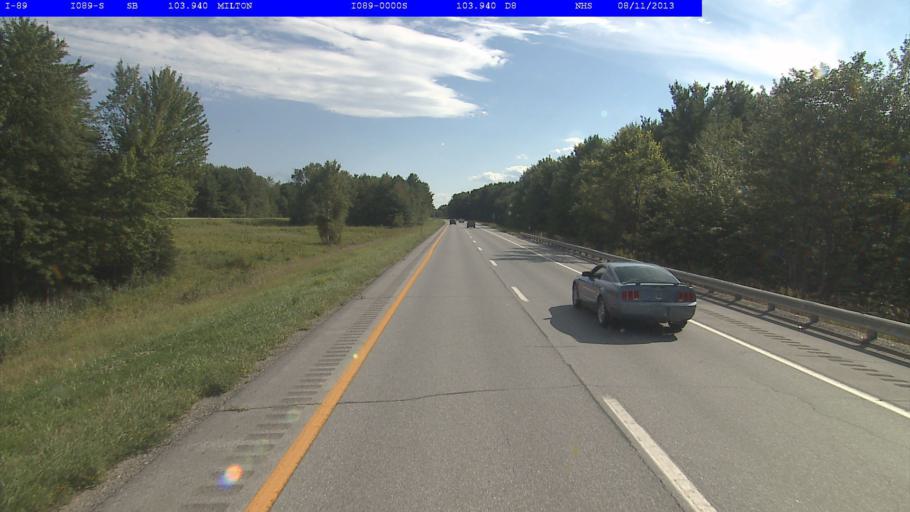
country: US
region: Vermont
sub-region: Chittenden County
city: Milton
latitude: 44.6697
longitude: -73.1343
